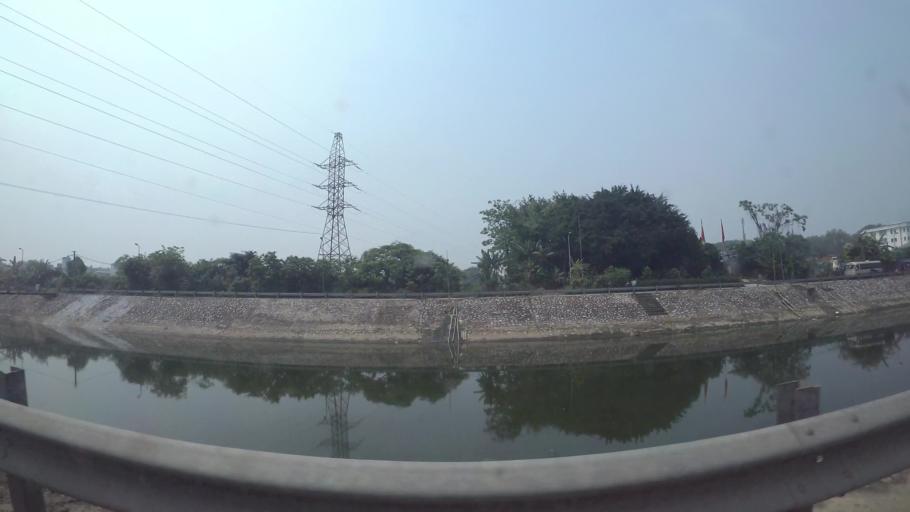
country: VN
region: Ha Noi
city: Van Dien
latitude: 20.9570
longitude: 105.8244
